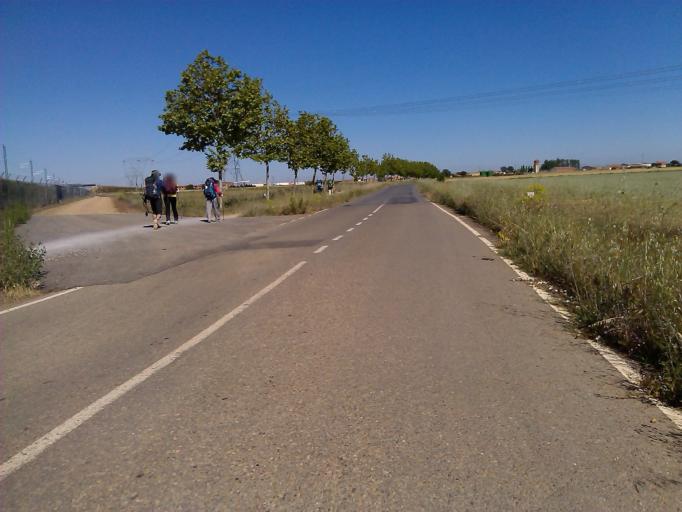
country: ES
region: Castille and Leon
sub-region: Provincia de Leon
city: Vallecillo
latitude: 42.4152
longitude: -5.2063
